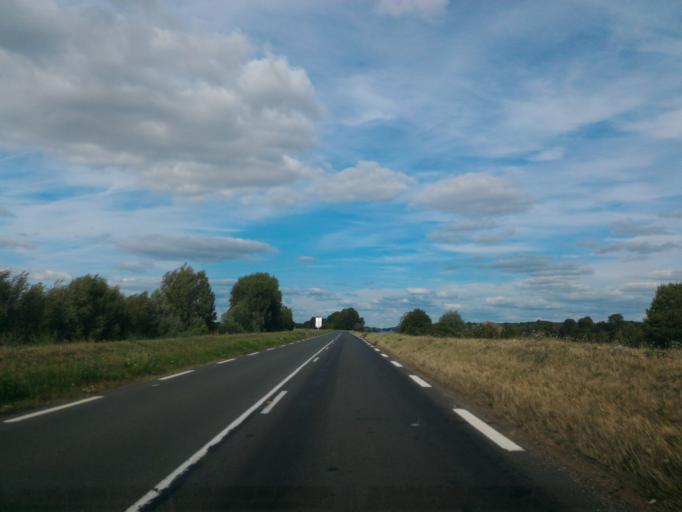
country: FR
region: Centre
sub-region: Departement du Loir-et-Cher
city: Onzain
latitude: 47.4729
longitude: 1.1307
